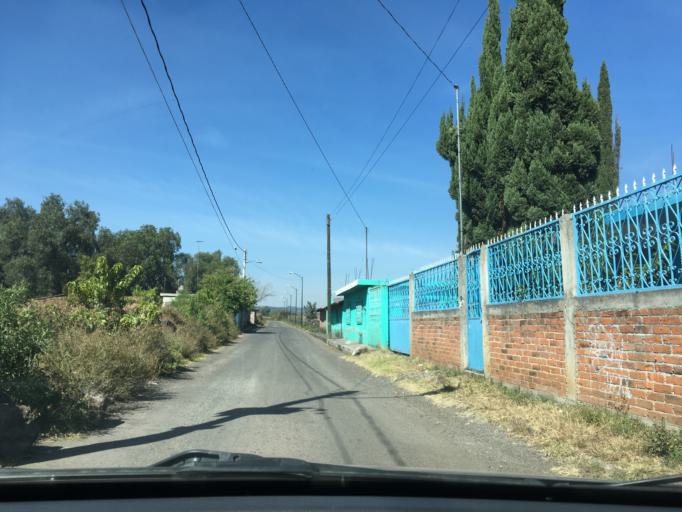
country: MX
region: Michoacan
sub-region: Morelia
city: Villa Magna
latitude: 19.6538
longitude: -101.3161
